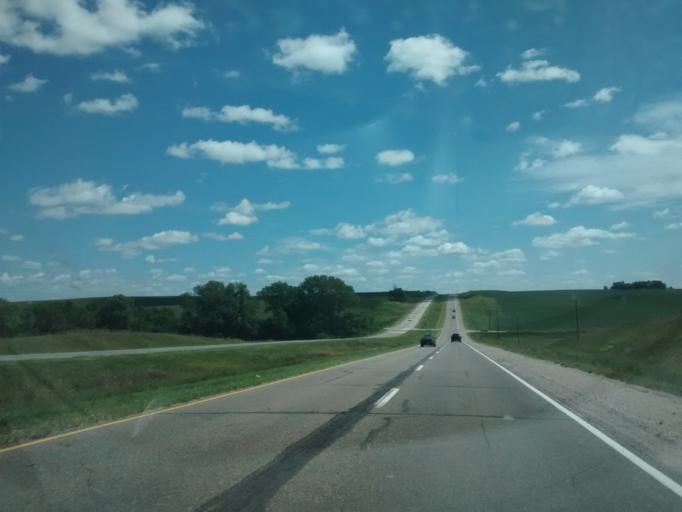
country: US
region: Iowa
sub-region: Woodbury County
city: Moville
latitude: 42.4749
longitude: -96.1585
